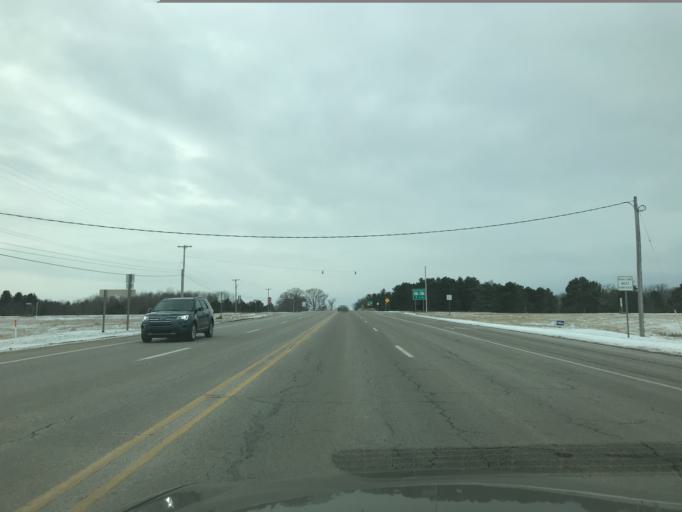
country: US
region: Michigan
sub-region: Roscommon County
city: Houghton Lake
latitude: 44.3359
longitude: -84.8036
